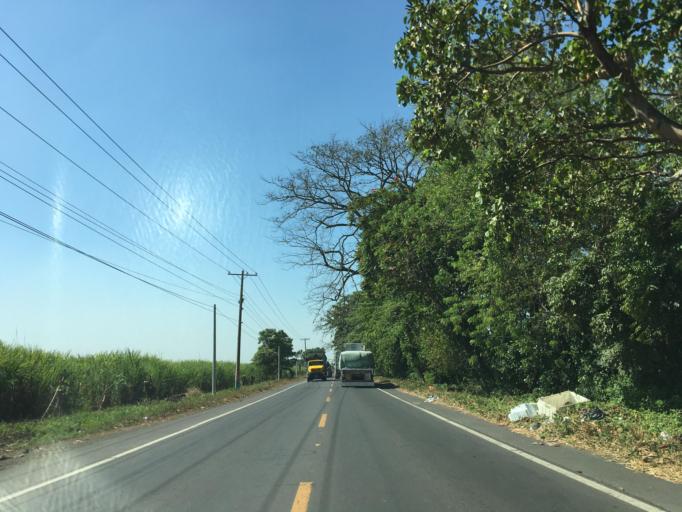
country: GT
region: Escuintla
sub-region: Municipio de Masagua
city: Masagua
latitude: 14.1946
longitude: -90.8549
